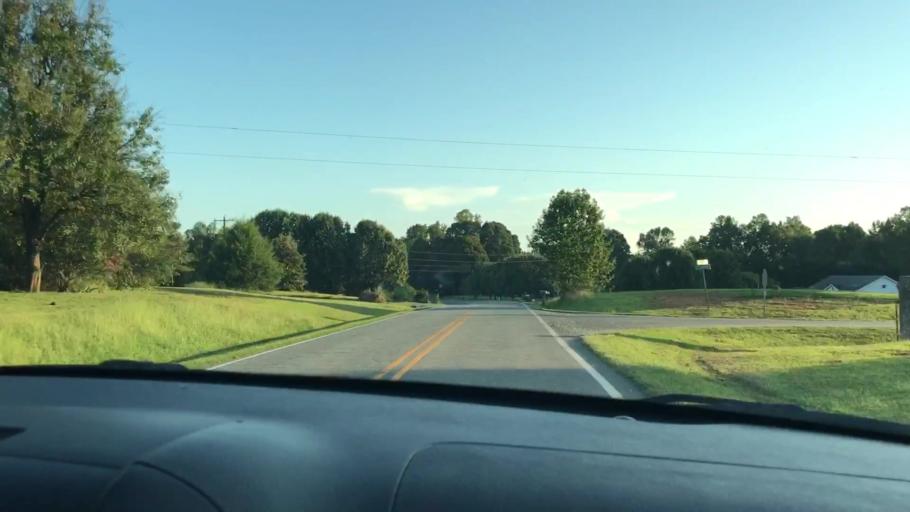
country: US
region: North Carolina
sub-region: Randolph County
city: Ramseur
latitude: 35.7930
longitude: -79.6441
